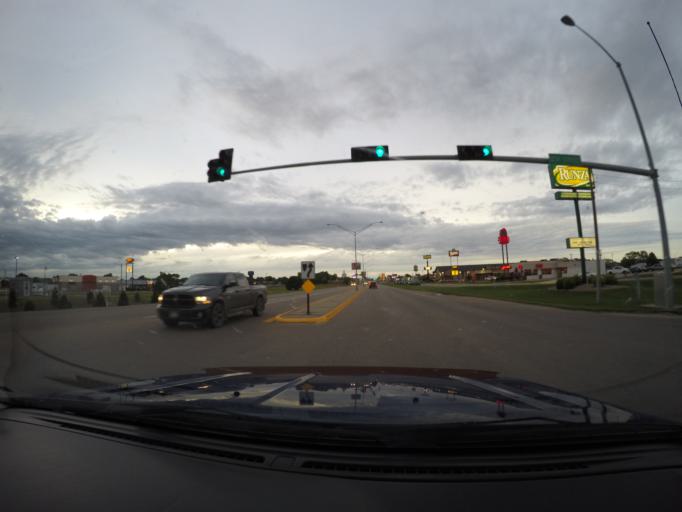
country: US
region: Nebraska
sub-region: Buffalo County
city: Kearney
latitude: 40.6820
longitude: -99.0848
